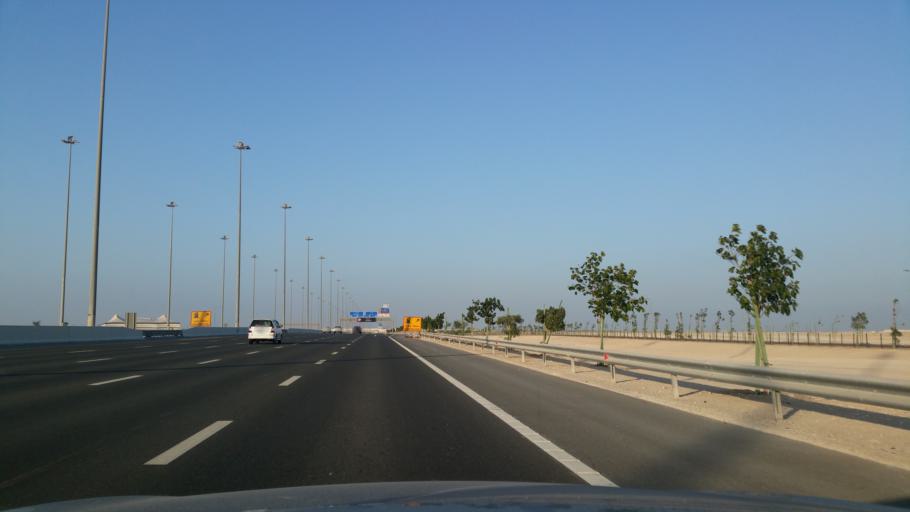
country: QA
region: Baladiyat az Za`ayin
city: Az Za`ayin
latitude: 25.6220
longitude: 51.4852
